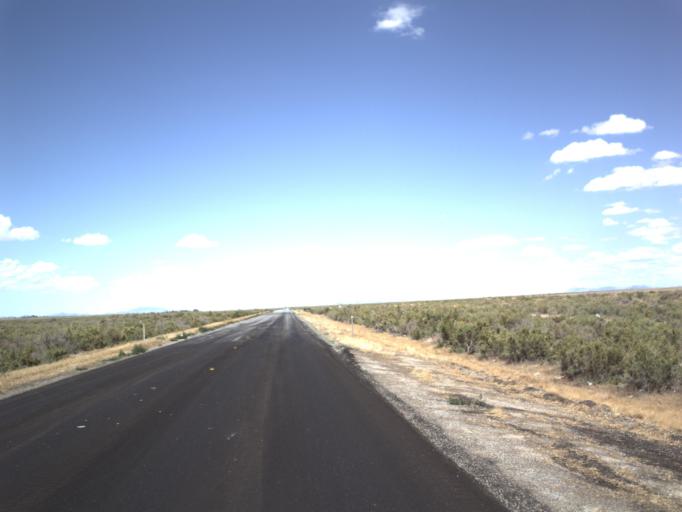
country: US
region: Utah
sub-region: Millard County
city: Delta
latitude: 39.3223
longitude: -112.4828
